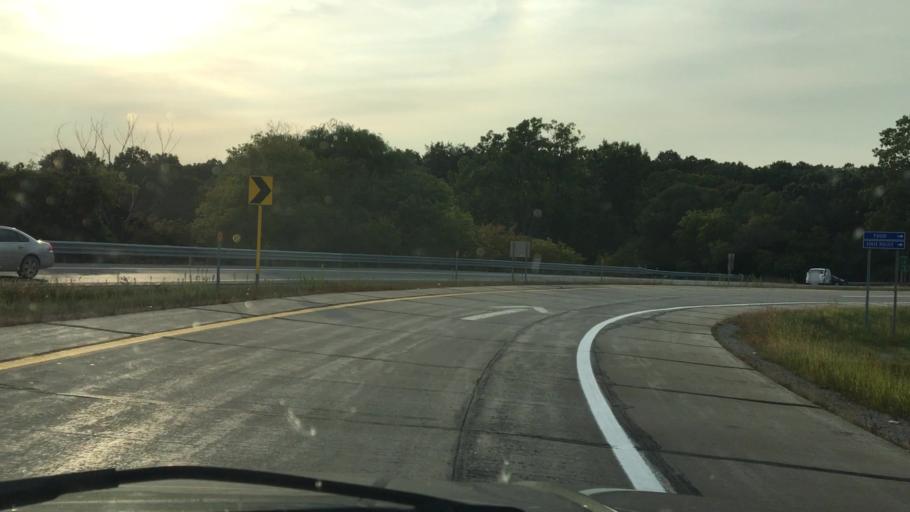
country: US
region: Michigan
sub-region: Livingston County
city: Brighton
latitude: 42.5306
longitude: -83.7671
